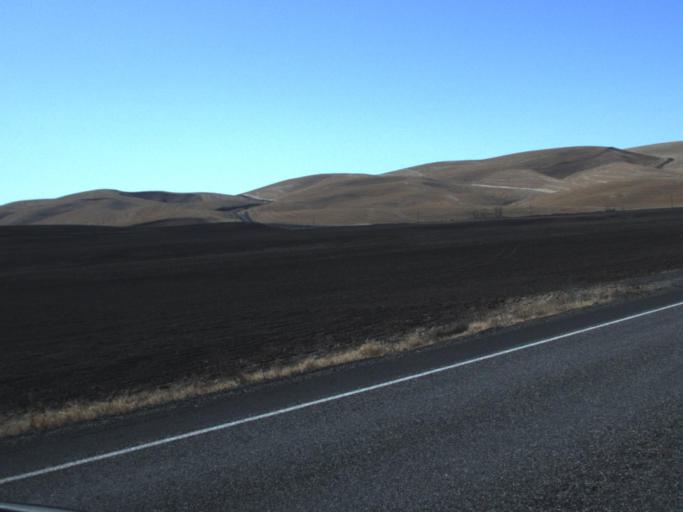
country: US
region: Washington
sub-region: Walla Walla County
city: Waitsburg
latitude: 46.2666
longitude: -118.2104
